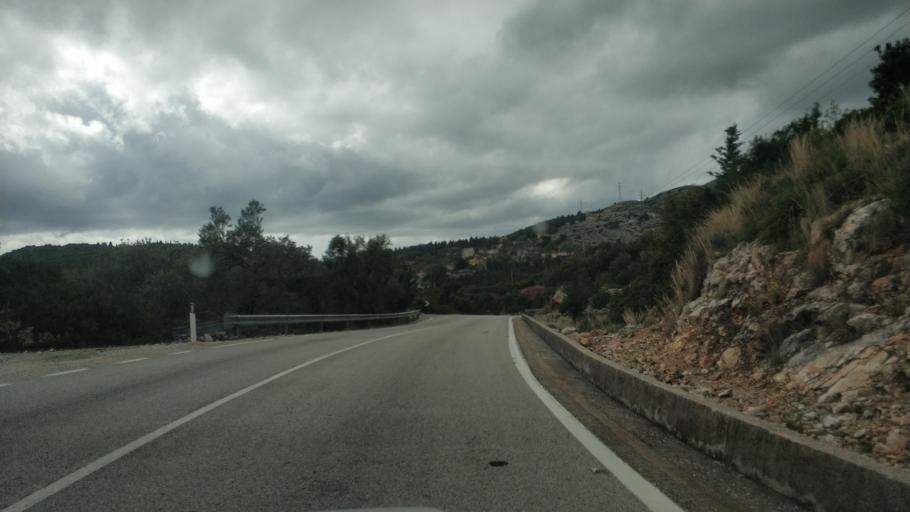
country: AL
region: Vlore
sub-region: Rrethi i Vlores
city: Vranisht
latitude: 40.1433
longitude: 19.6808
